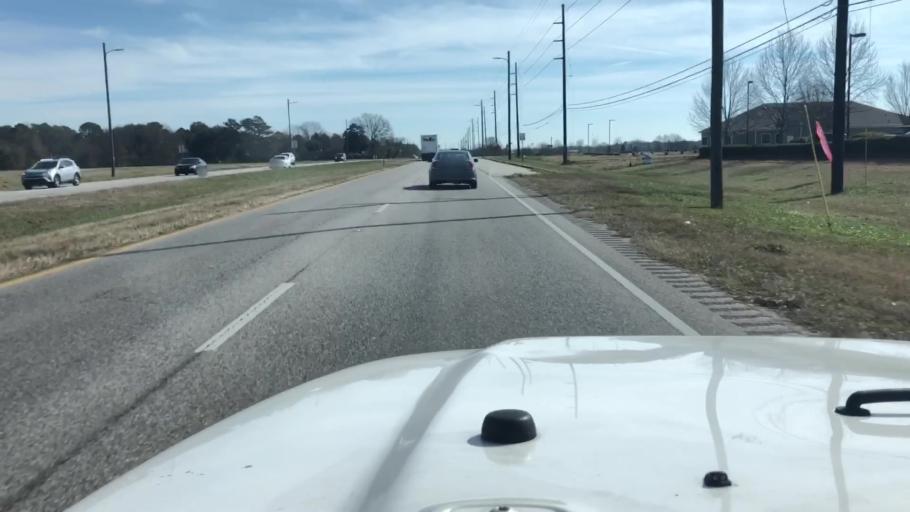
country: US
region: Alabama
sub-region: Montgomery County
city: Pike Road
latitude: 32.3788
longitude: -86.1562
